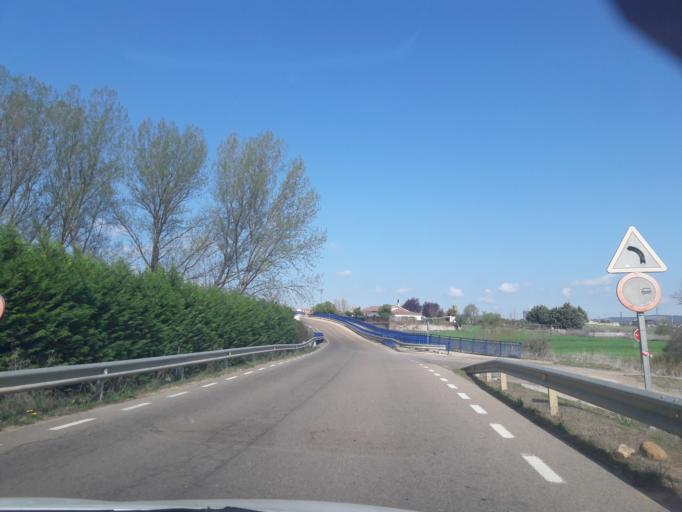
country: ES
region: Castille and Leon
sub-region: Provincia de Salamanca
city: Ciudad Rodrigo
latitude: 40.5933
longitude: -6.5163
